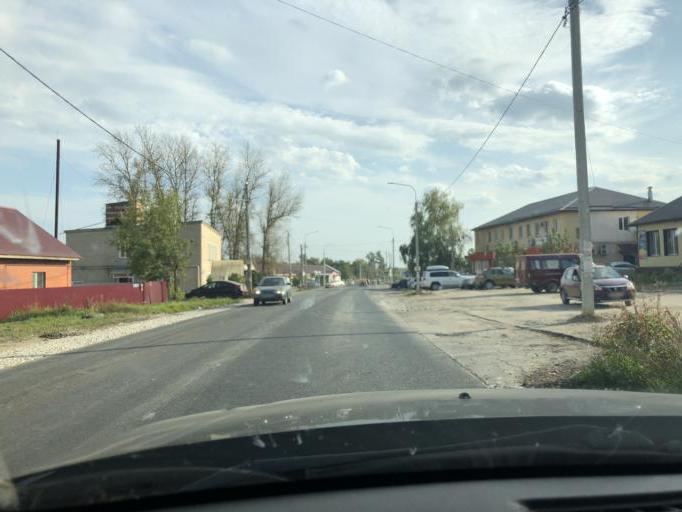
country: RU
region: Tula
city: Leninskiy
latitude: 54.2873
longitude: 37.4661
